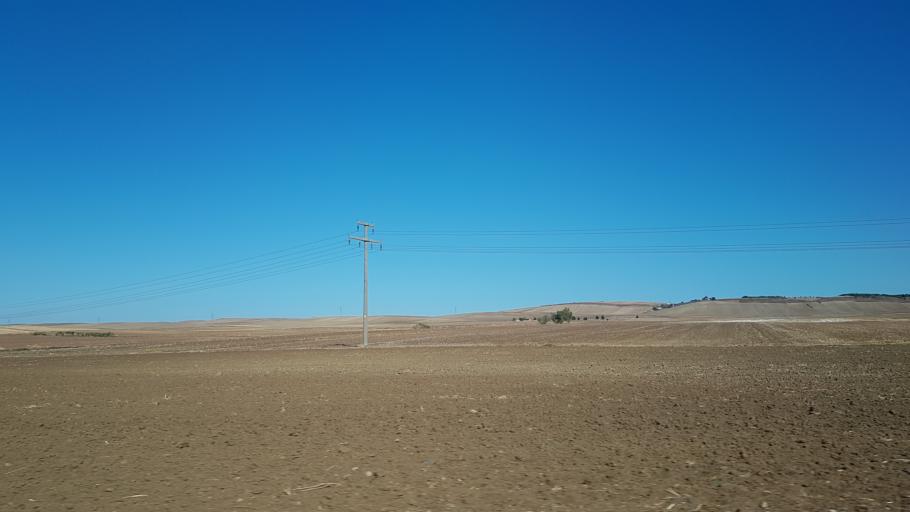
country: TR
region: Tekirdag
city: Corlu
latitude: 41.0122
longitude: 27.8015
